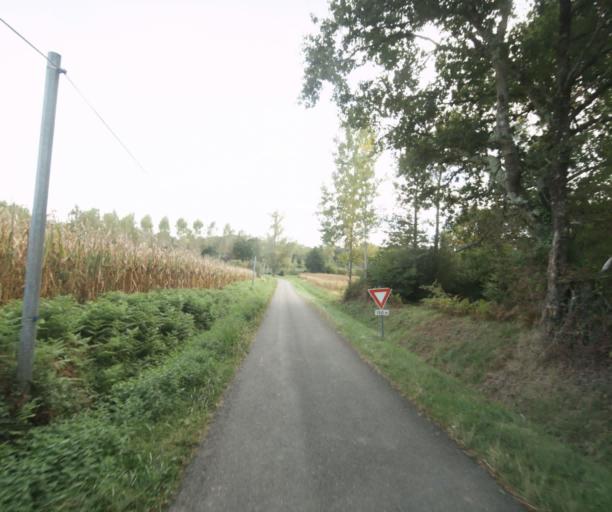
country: FR
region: Midi-Pyrenees
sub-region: Departement du Gers
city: Cazaubon
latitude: 43.8651
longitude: -0.1201
